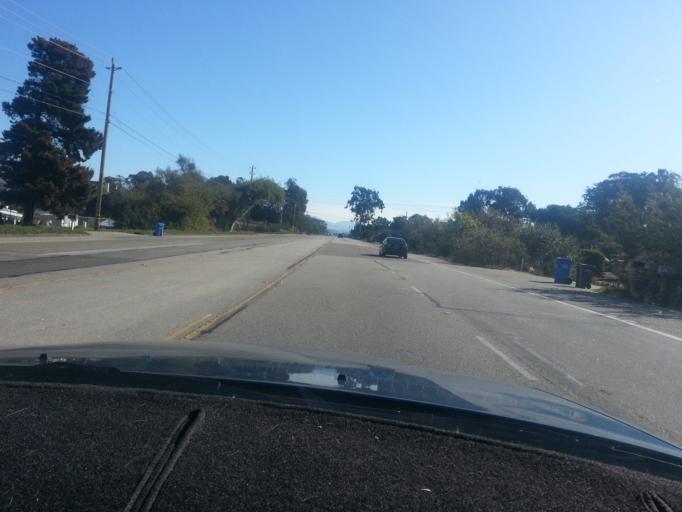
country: US
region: California
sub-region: San Luis Obispo County
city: Los Osos
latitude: 35.3088
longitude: -120.8228
